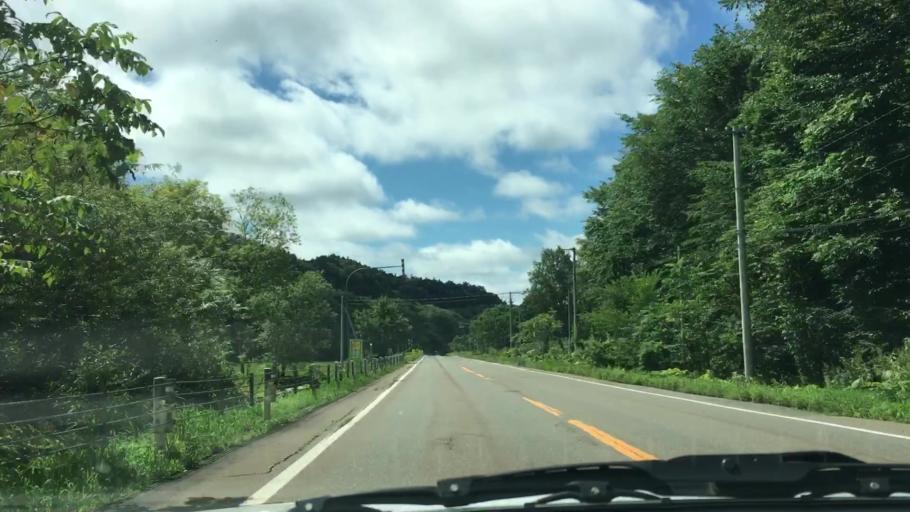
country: JP
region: Hokkaido
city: Kitami
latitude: 43.3742
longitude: 143.8747
